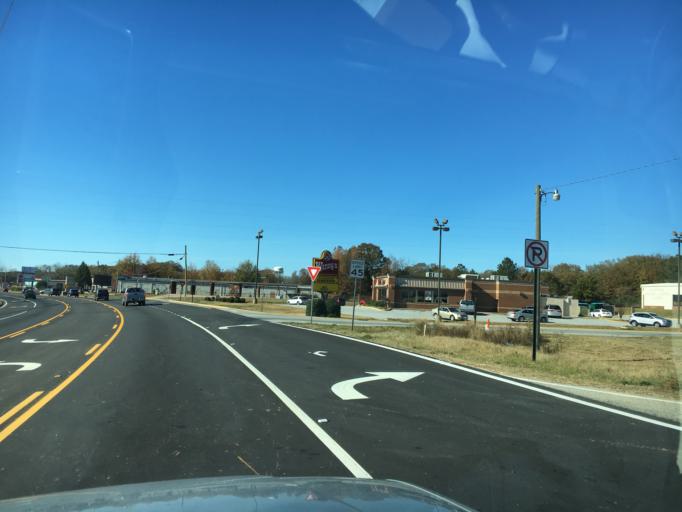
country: US
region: Georgia
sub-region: Hart County
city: Hartwell
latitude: 34.3543
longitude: -82.9078
